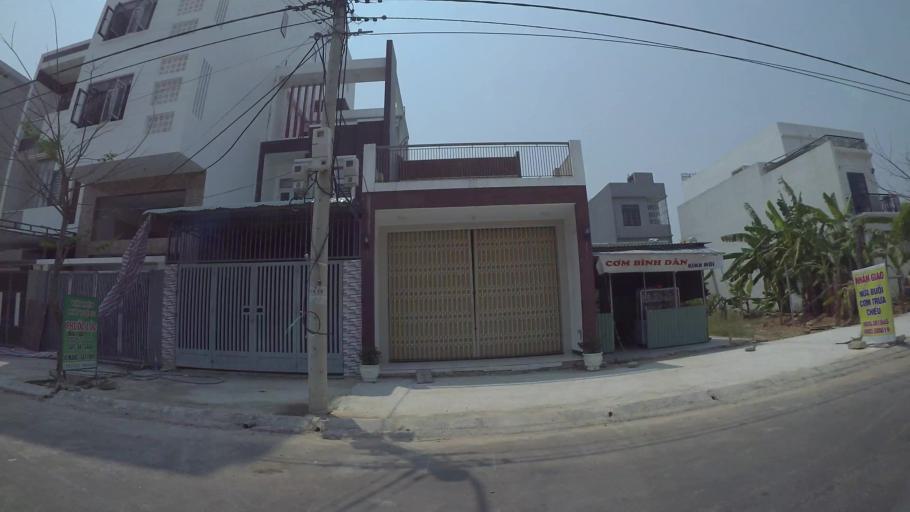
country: VN
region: Da Nang
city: Cam Le
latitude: 16.0157
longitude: 108.2224
